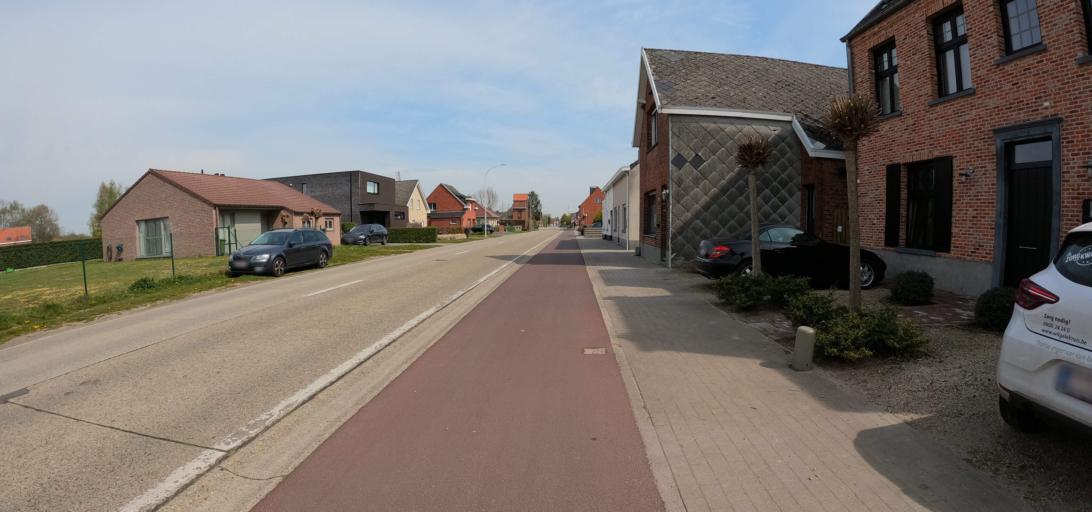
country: BE
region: Flanders
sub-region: Provincie Antwerpen
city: Zandhoven
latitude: 51.2225
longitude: 4.6952
